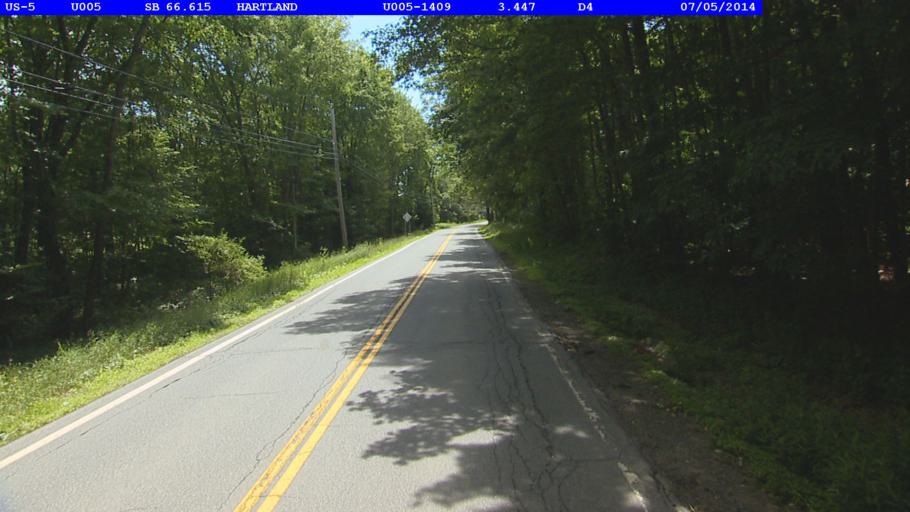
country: US
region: Vermont
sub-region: Windsor County
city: Windsor
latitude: 43.5616
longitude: -72.3864
